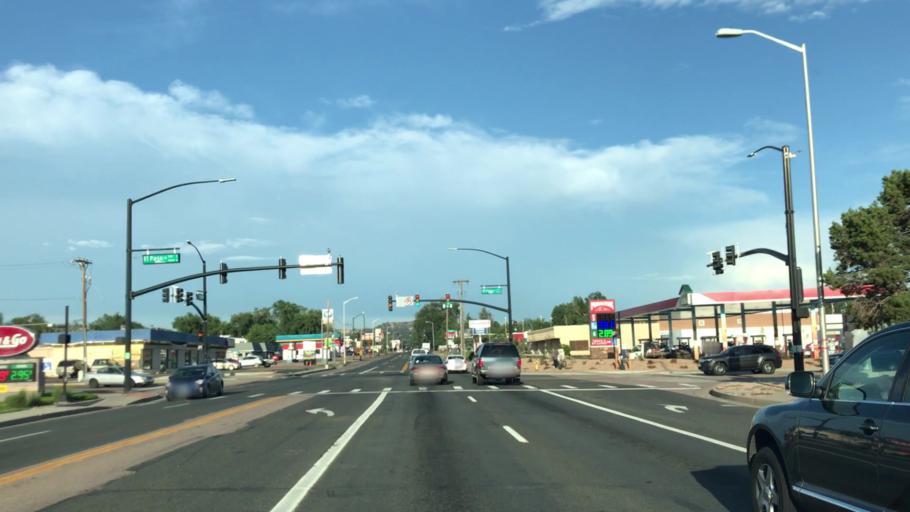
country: US
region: Colorado
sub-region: El Paso County
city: Colorado Springs
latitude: 38.8742
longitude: -104.8136
